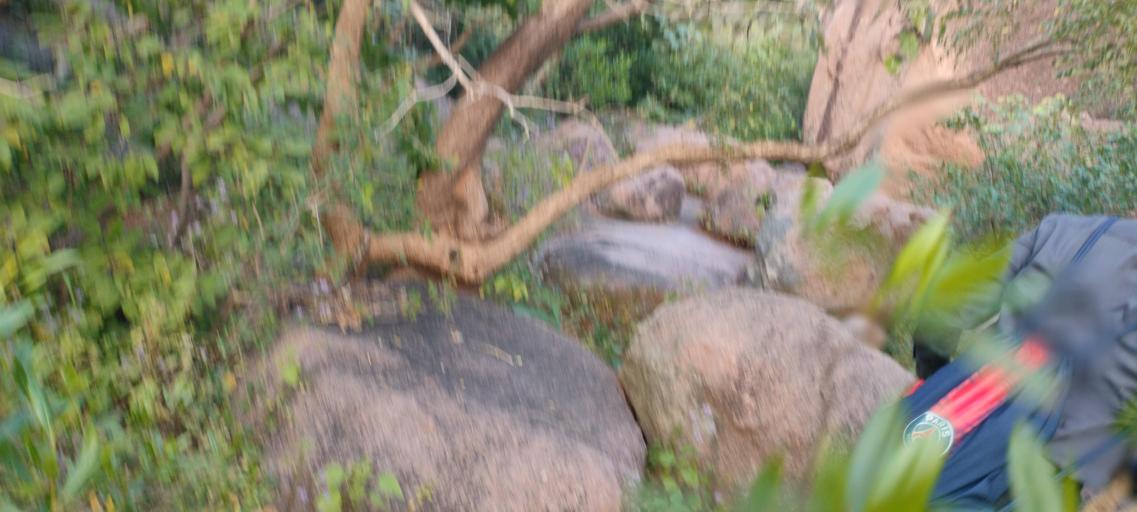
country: IN
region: Telangana
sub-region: Mahbubnagar
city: Farrukhnagar
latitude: 16.8973
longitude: 78.4912
